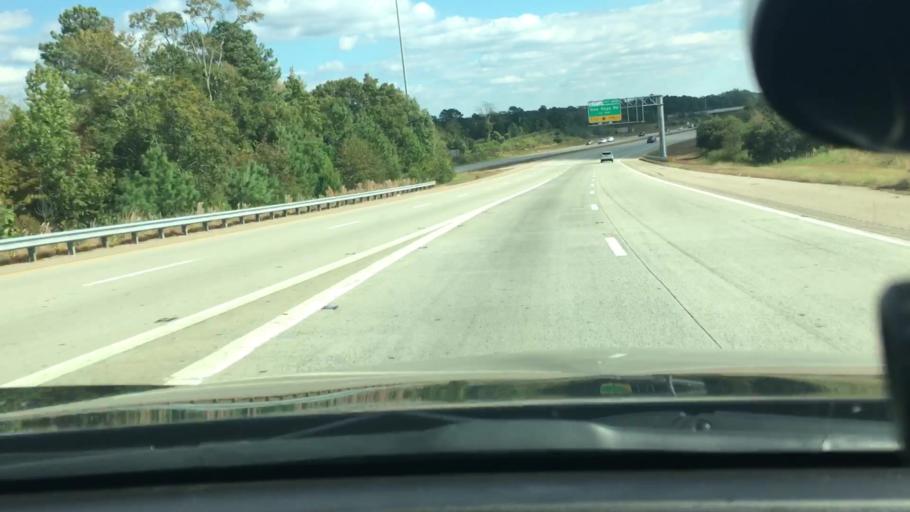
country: US
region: North Carolina
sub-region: Wake County
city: Raleigh
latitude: 35.7799
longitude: -78.5691
